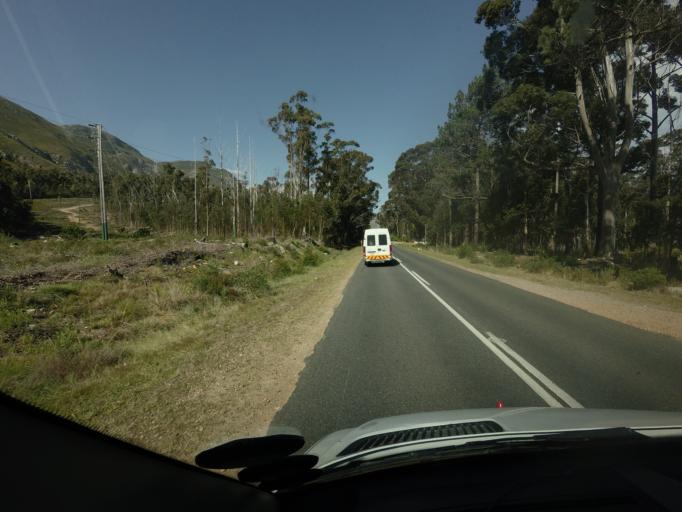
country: ZA
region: Western Cape
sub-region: Overberg District Municipality
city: Hermanus
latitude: -34.4059
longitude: 19.3569
